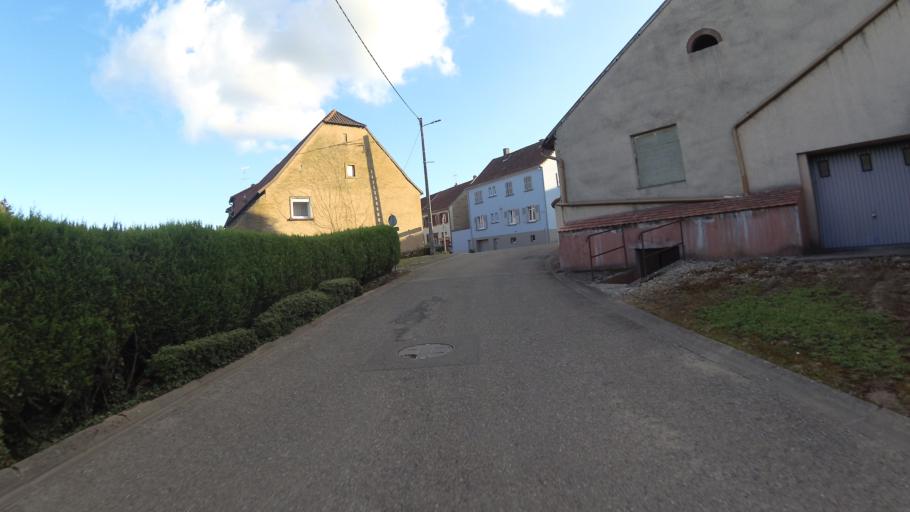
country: FR
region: Alsace
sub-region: Departement du Bas-Rhin
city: Oermingen
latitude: 48.9980
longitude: 7.1291
